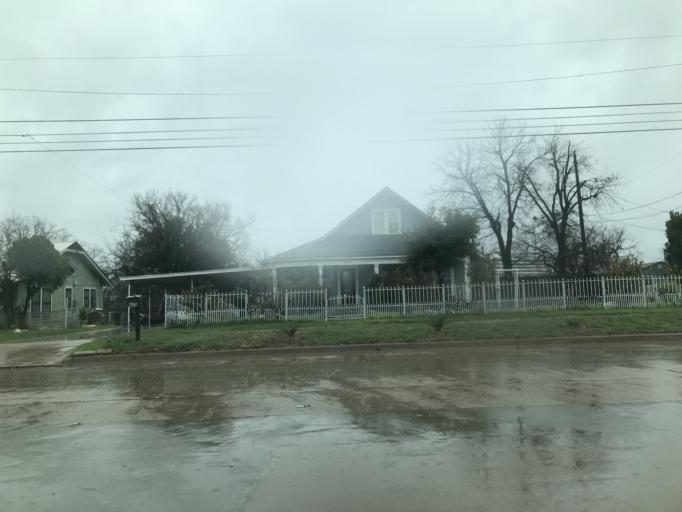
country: US
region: Texas
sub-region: Tom Green County
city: San Angelo
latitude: 31.4654
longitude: -100.4271
